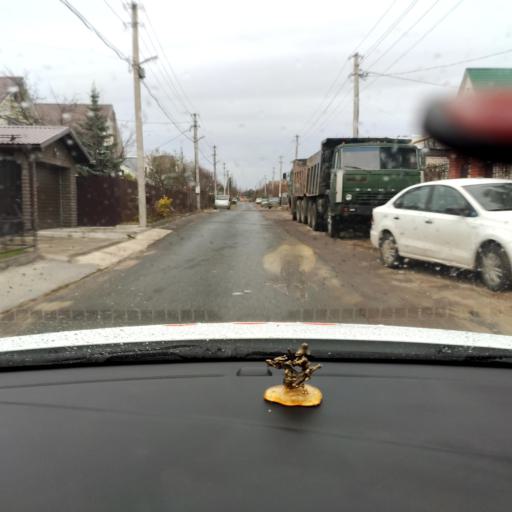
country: RU
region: Tatarstan
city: Vysokaya Gora
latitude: 55.8443
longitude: 49.2387
